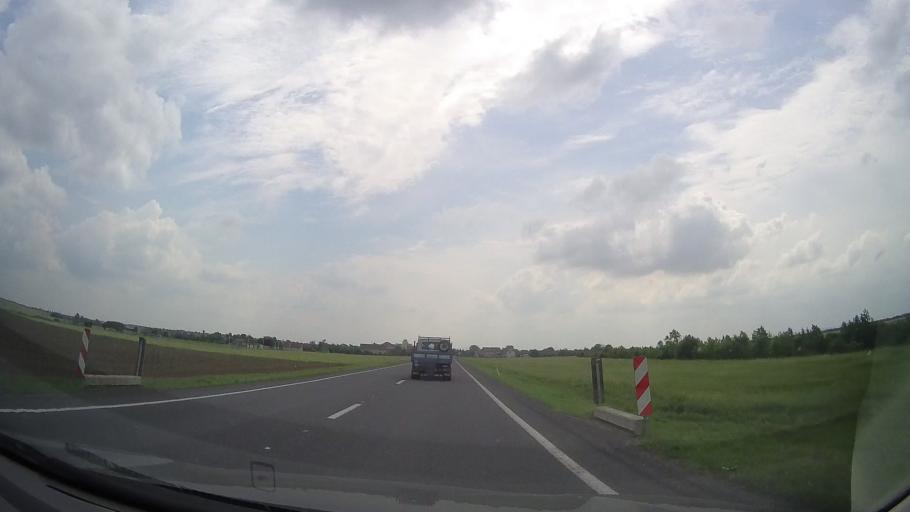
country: RO
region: Timis
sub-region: Comuna Topolovatu Mare
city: Topolovatu Mare
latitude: 45.7794
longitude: 21.6084
